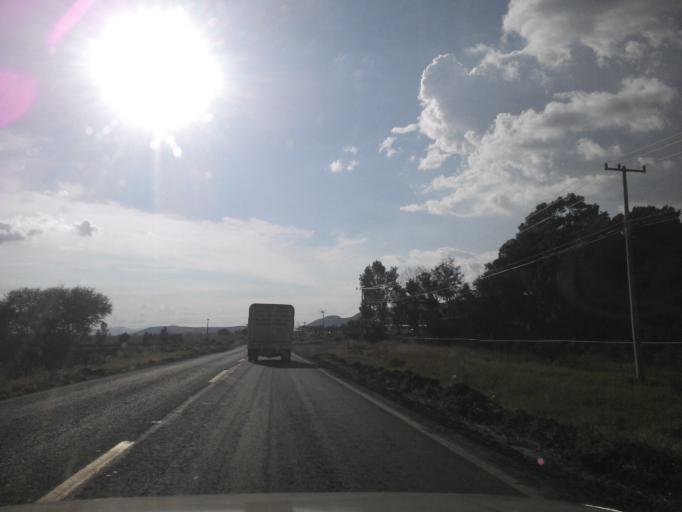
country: MX
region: Jalisco
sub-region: Atotonilco el Alto
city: San Francisco de Asis
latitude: 20.5419
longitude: -102.5828
